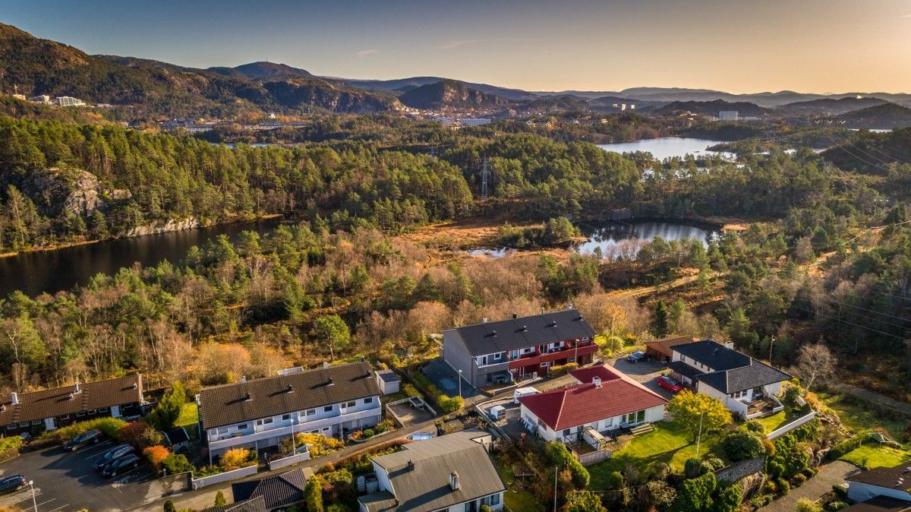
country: NO
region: Hordaland
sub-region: Askoy
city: Askoy
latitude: 60.3681
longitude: 5.2004
